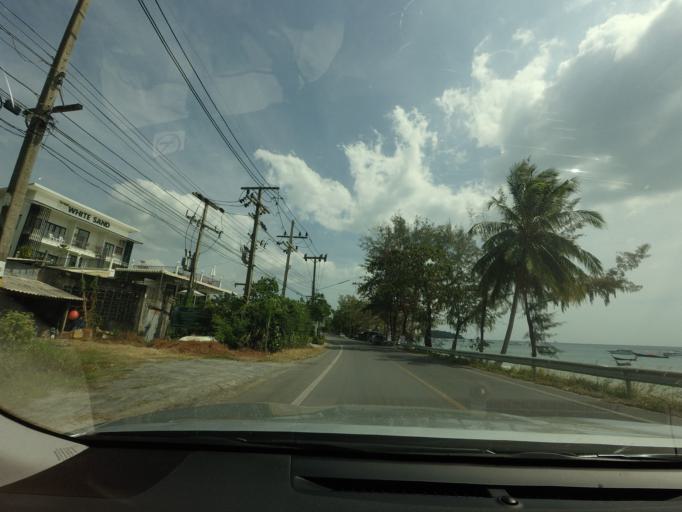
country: TH
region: Phangnga
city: Ban Ao Nang
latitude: 8.0653
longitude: 98.7440
